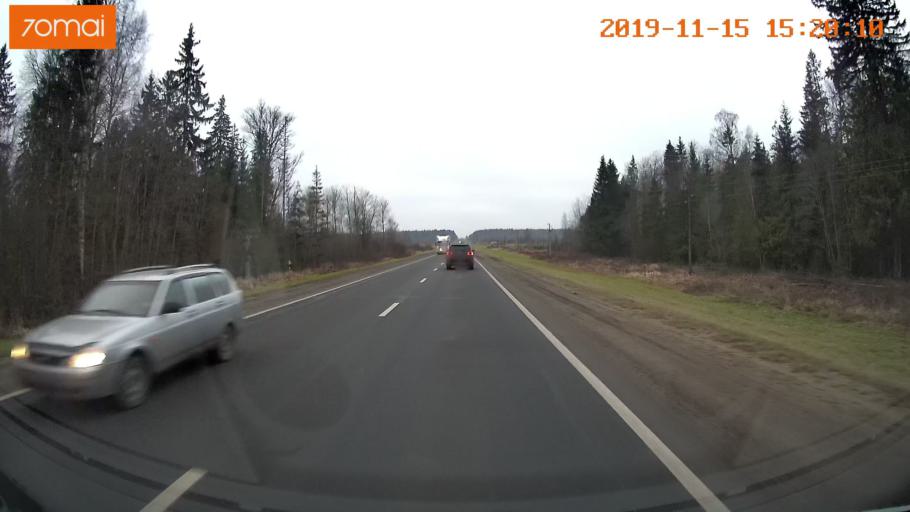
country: RU
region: Jaroslavl
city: Danilov
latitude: 58.2265
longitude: 40.1661
